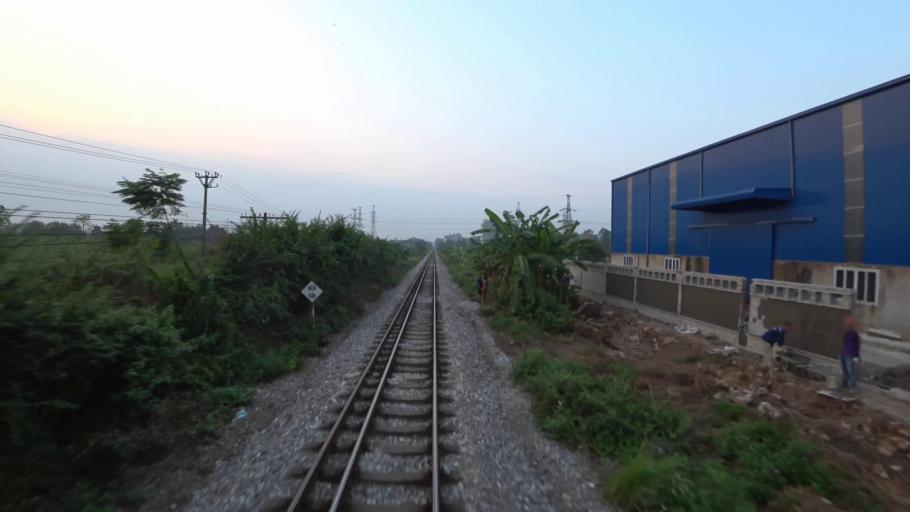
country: VN
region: Ha Noi
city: Dong Anh
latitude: 21.1467
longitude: 105.8596
